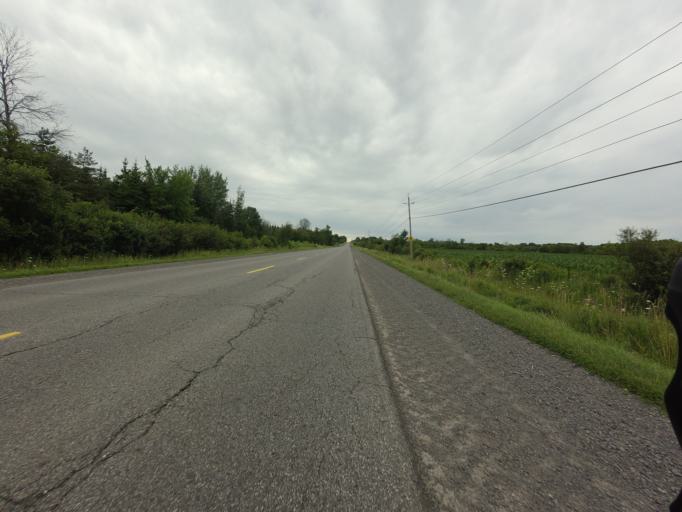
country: CA
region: Ontario
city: Ottawa
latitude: 45.2694
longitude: -75.6423
